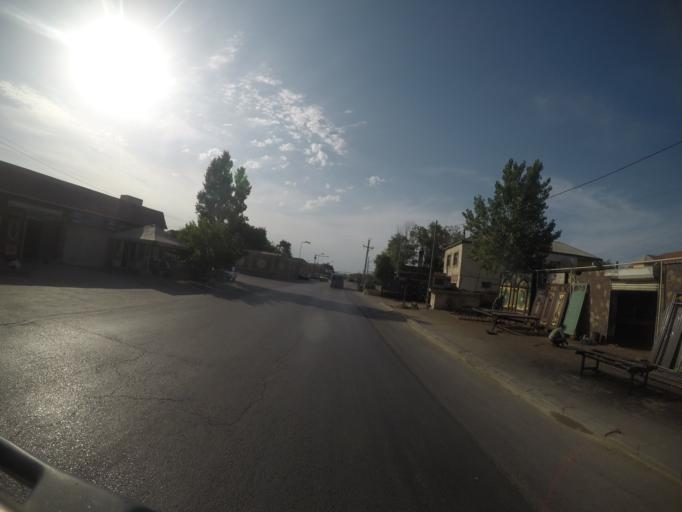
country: AZ
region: Baki
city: Binagadi
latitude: 40.4717
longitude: 49.8365
